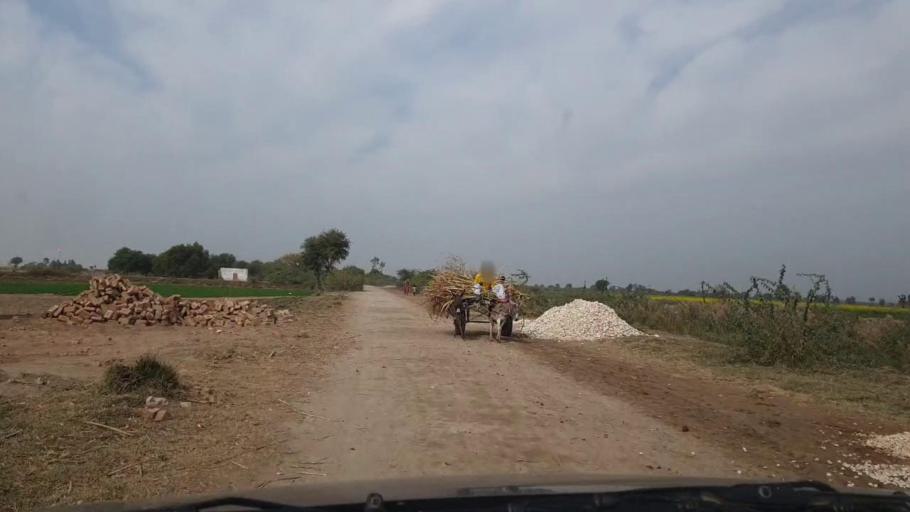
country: PK
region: Sindh
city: Sanghar
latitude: 26.0912
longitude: 68.8956
